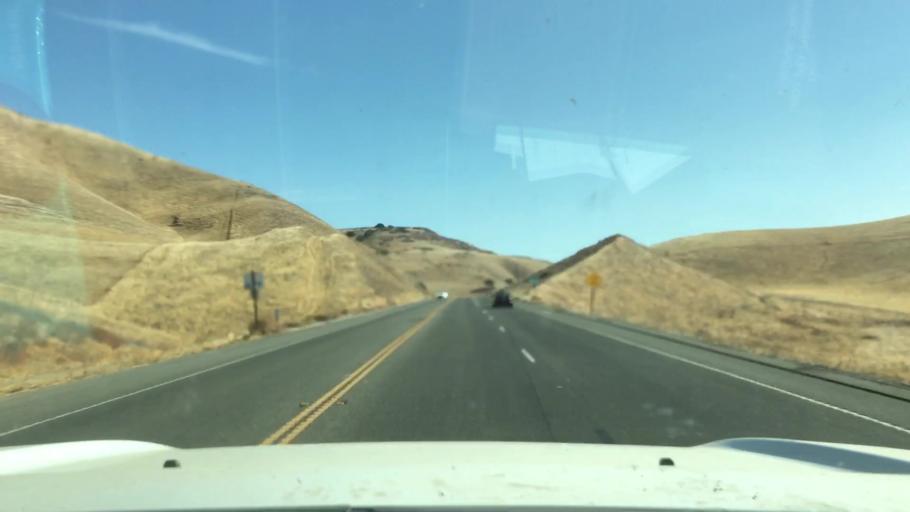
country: US
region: California
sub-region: San Luis Obispo County
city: Shandon
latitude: 35.7436
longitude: -120.2198
